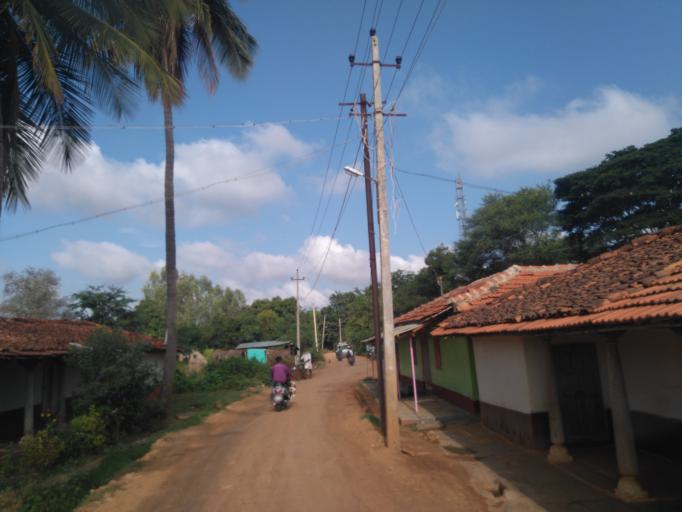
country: IN
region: Karnataka
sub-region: Mysore
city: Tirumakudal Narsipur
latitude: 12.2593
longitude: 76.9734
